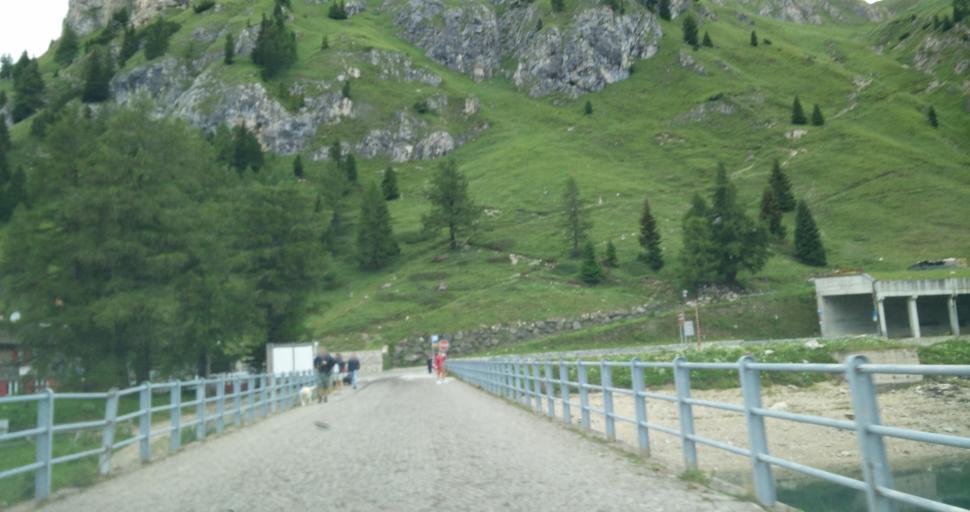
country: IT
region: Trentino-Alto Adige
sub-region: Bolzano
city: Corvara in Badia
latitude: 46.4633
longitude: 11.8627
